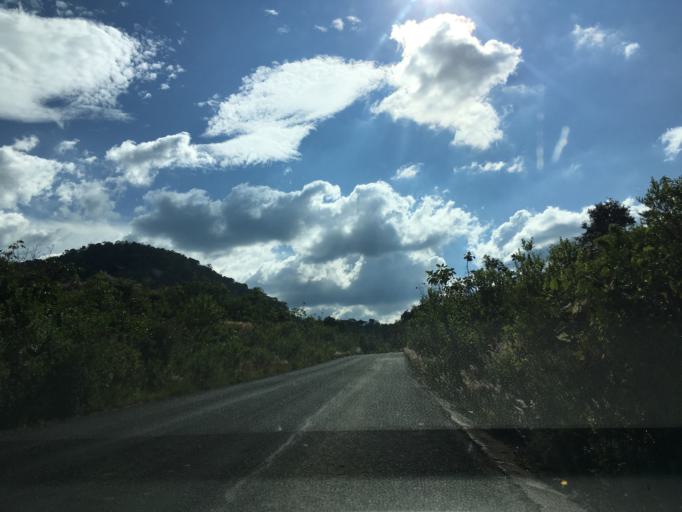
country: MX
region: Michoacan
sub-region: Zacapu
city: Naranja de Tapia
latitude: 19.7507
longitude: -101.7851
